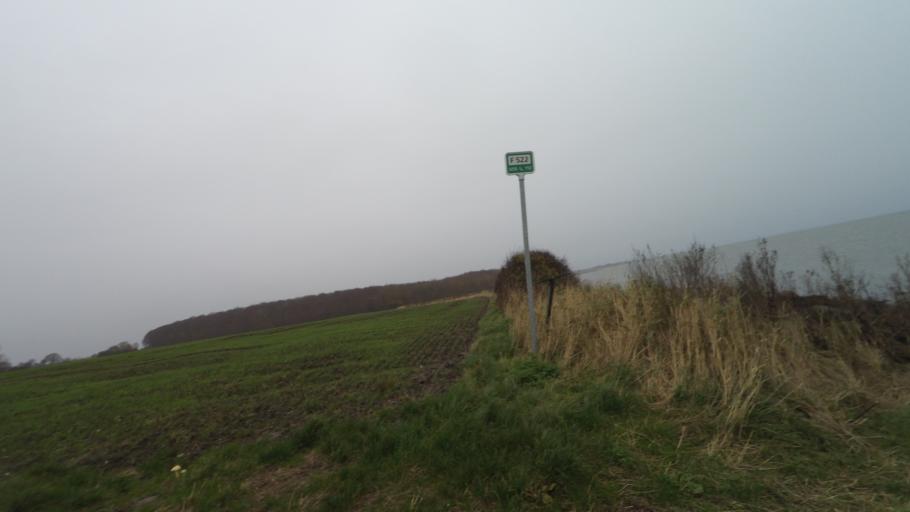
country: DK
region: Central Jutland
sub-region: Odder Kommune
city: Odder
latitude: 55.8973
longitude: 10.2228
